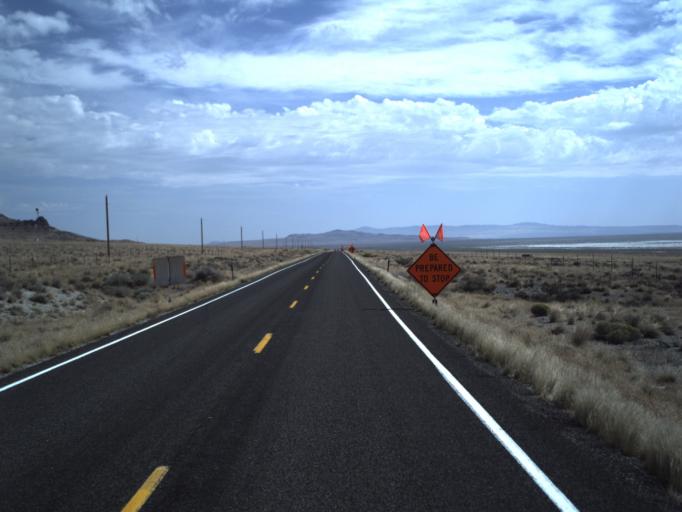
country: US
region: Utah
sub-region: Tooele County
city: Wendover
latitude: 41.4391
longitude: -113.7209
